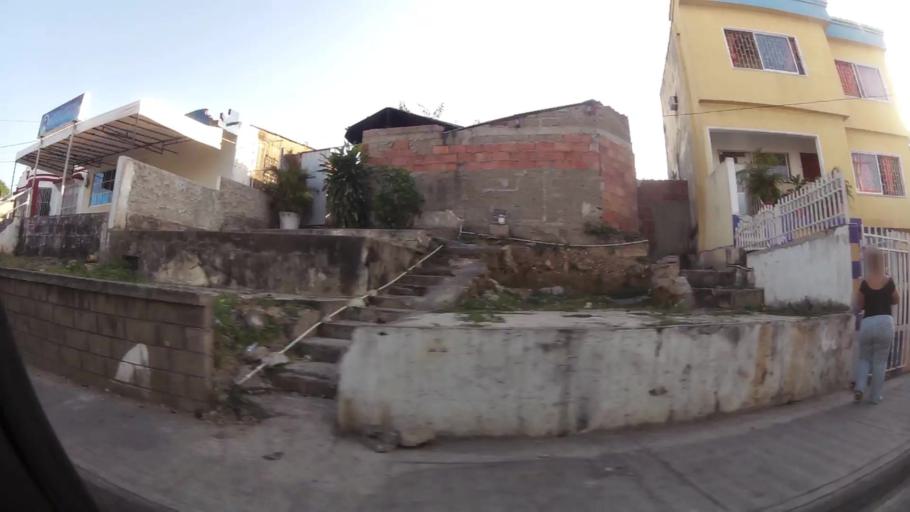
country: CO
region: Bolivar
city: Cartagena
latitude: 10.3968
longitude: -75.4786
